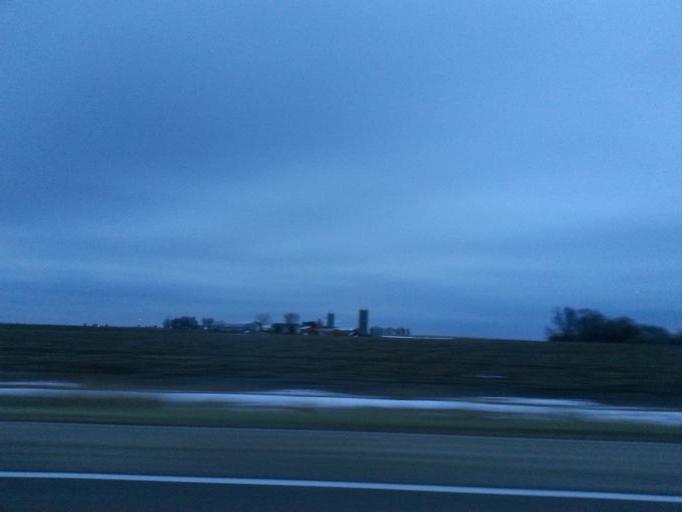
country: US
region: Iowa
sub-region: Black Hawk County
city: La Porte City
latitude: 42.3914
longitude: -92.1360
